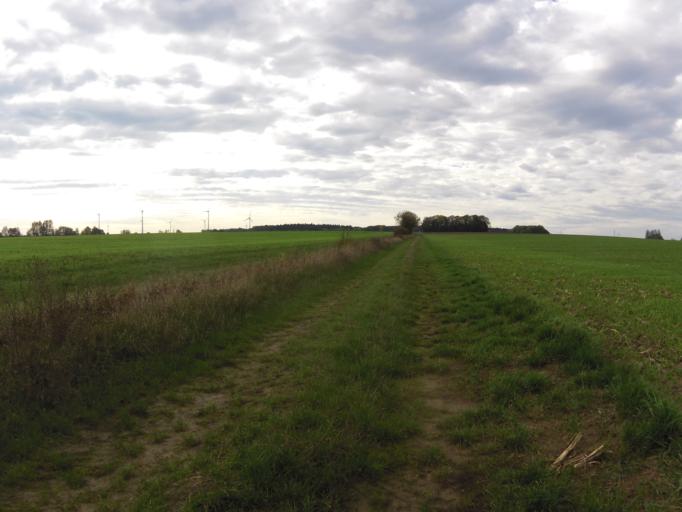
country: DE
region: Bavaria
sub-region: Regierungsbezirk Unterfranken
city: Biebelried
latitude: 49.7305
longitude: 10.0823
